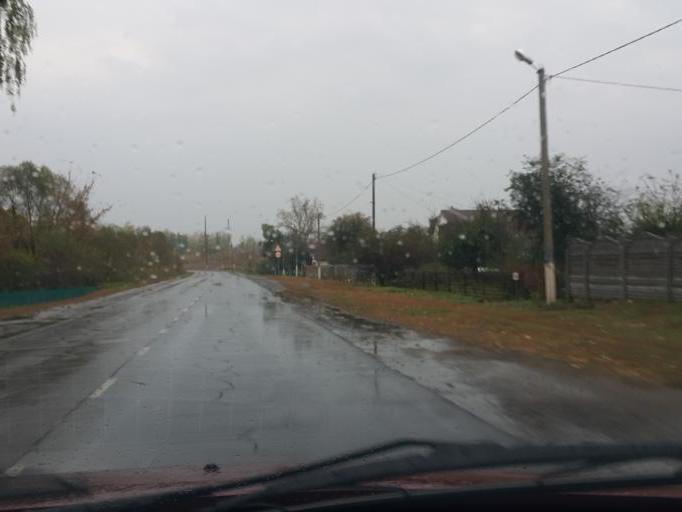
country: RU
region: Tambov
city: Znamenka
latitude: 52.4075
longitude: 41.4577
